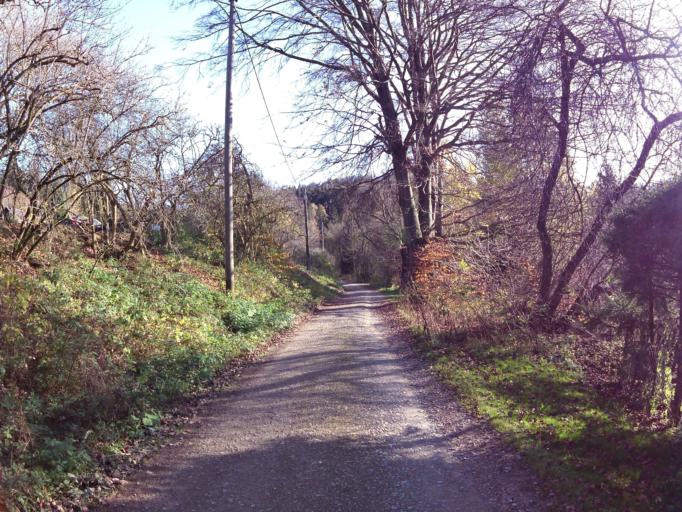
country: DE
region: Thuringia
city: Ruhla
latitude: 50.8833
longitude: 10.3940
